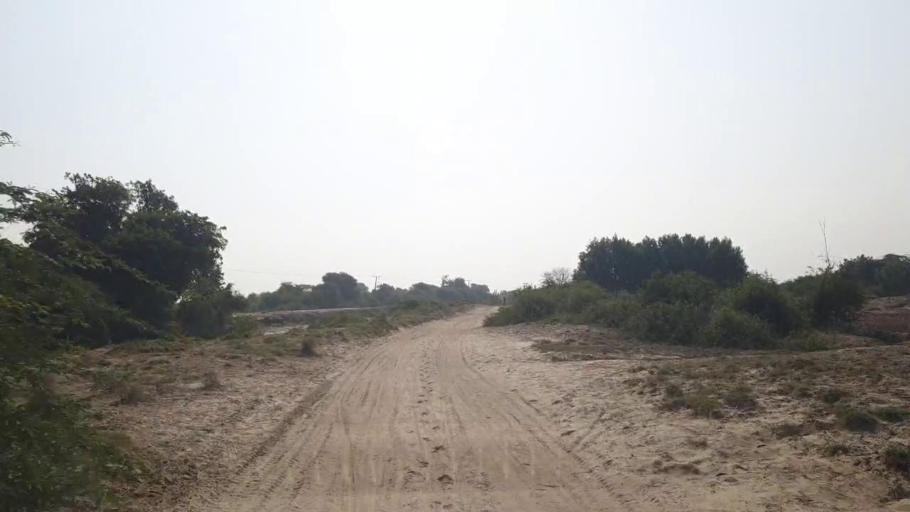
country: PK
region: Sindh
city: Matli
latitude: 24.9548
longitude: 68.6025
